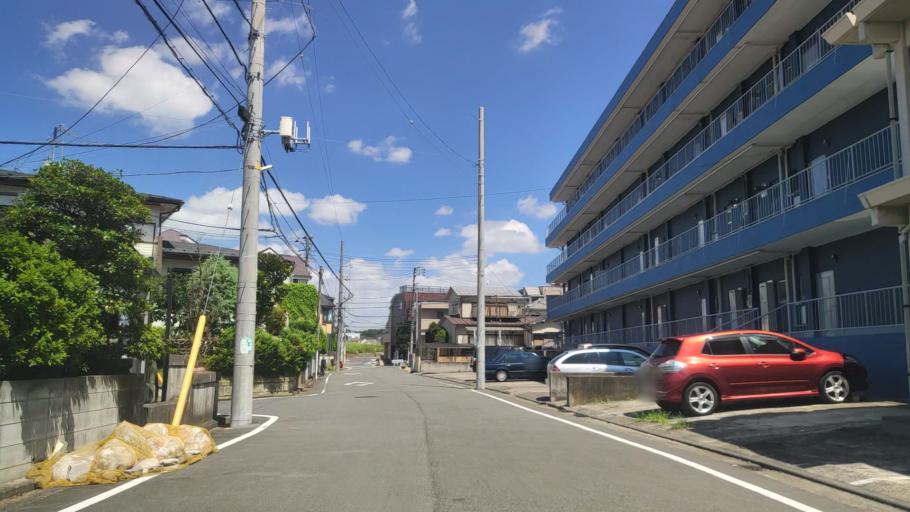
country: JP
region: Kanagawa
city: Yokohama
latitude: 35.5319
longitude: 139.6266
